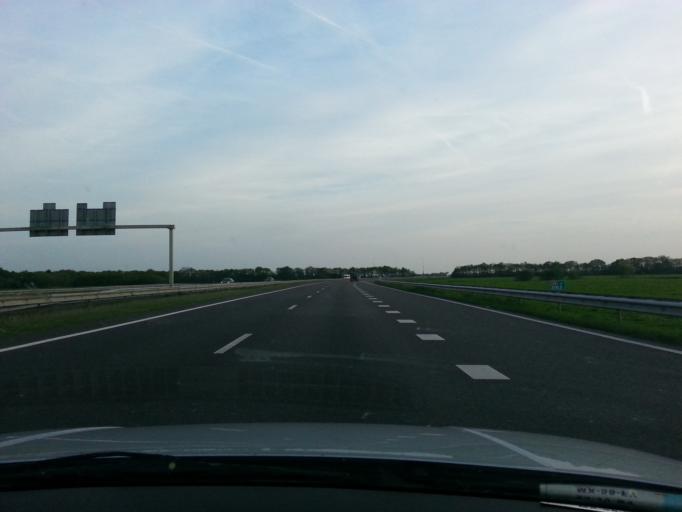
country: NL
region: Friesland
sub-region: Gemeente Skarsterlan
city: Joure
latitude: 52.9539
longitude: 5.8130
